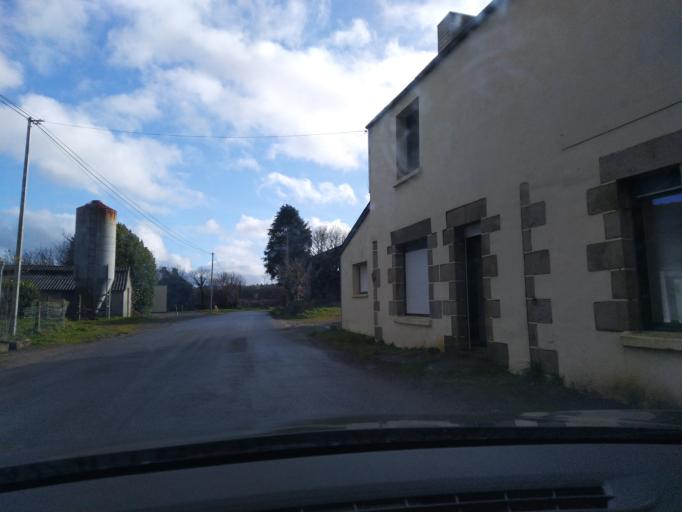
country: FR
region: Brittany
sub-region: Departement du Finistere
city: Guerlesquin
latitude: 48.4879
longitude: -3.5843
